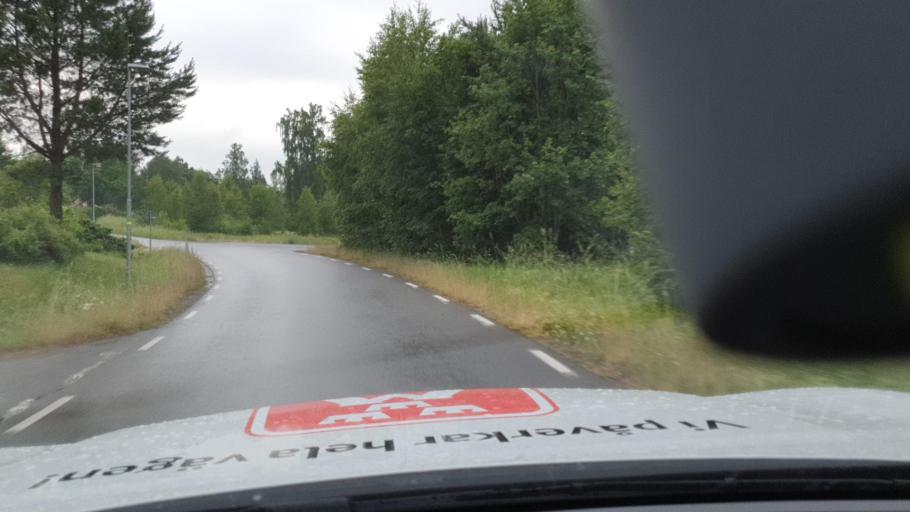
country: SE
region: Vaestra Goetaland
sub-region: Skovde Kommun
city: Stopen
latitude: 58.4601
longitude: 13.9165
